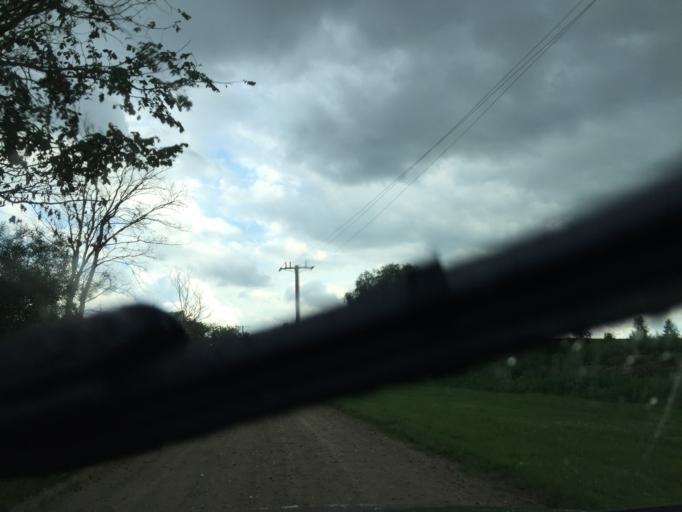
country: LV
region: Dobeles Rajons
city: Dobele
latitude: 56.6141
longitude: 23.3326
